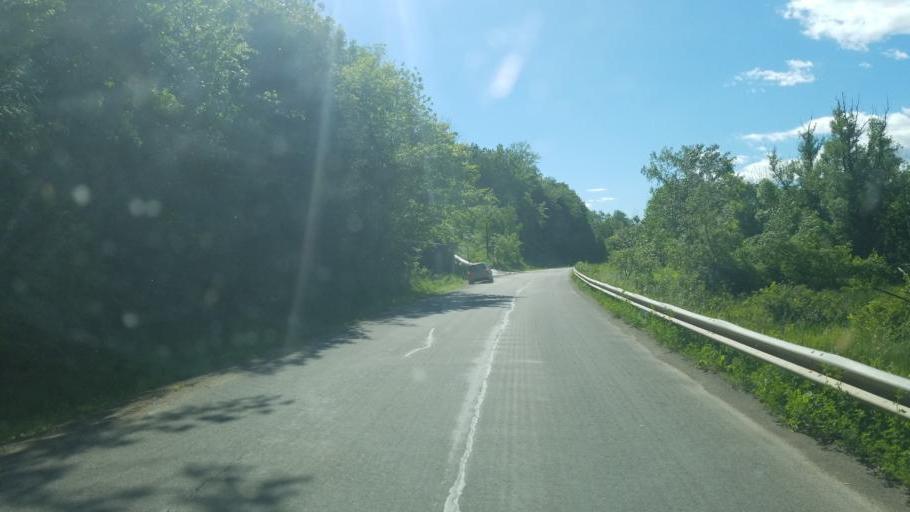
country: US
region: New York
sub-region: Montgomery County
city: Saint Johnsville
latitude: 42.9911
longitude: -74.7259
